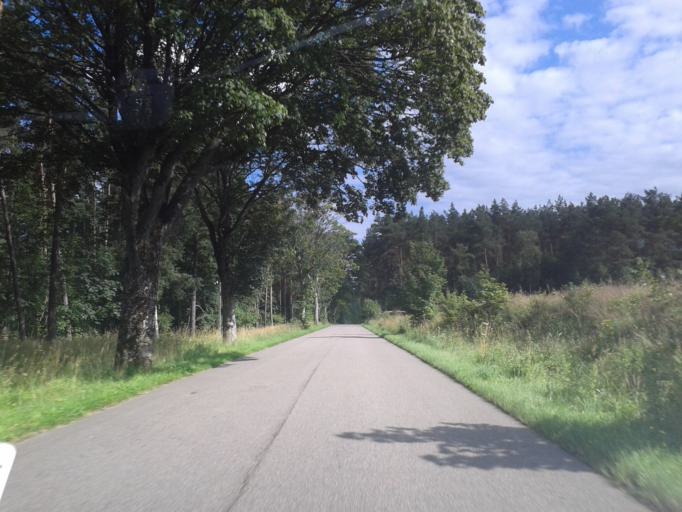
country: PL
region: West Pomeranian Voivodeship
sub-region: Powiat szczecinecki
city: Lubowo
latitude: 53.6402
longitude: 16.3262
